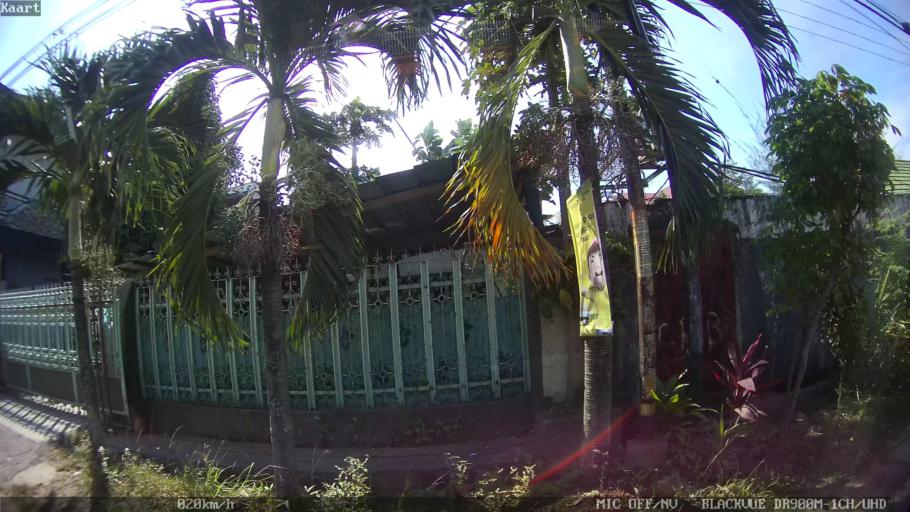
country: ID
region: Lampung
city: Kedaton
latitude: -5.3690
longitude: 105.2480
